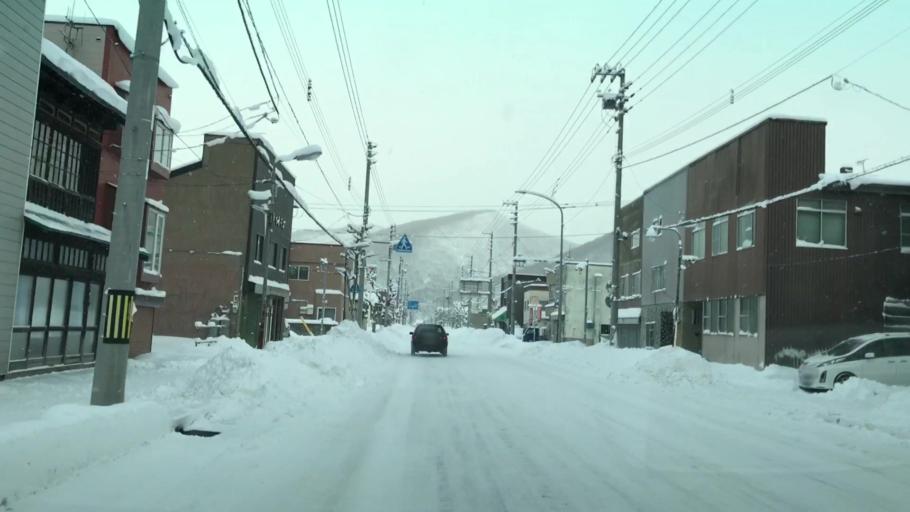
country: JP
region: Hokkaido
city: Yoichi
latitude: 43.2053
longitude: 140.7714
